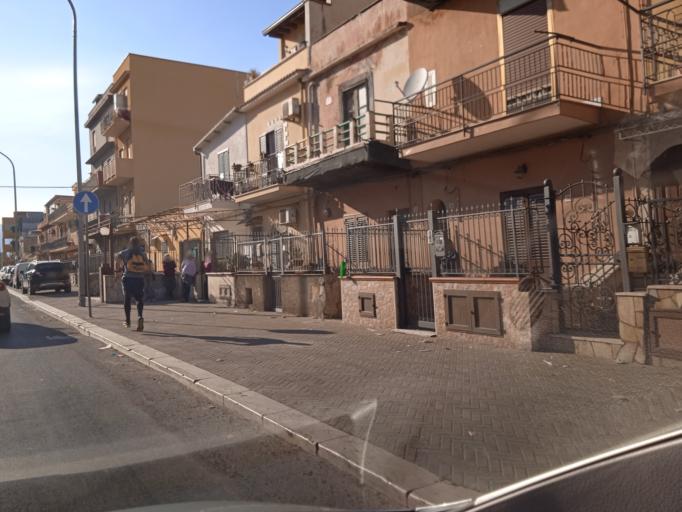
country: IT
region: Sicily
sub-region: Palermo
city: Ciaculli
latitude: 38.0976
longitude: 13.4163
